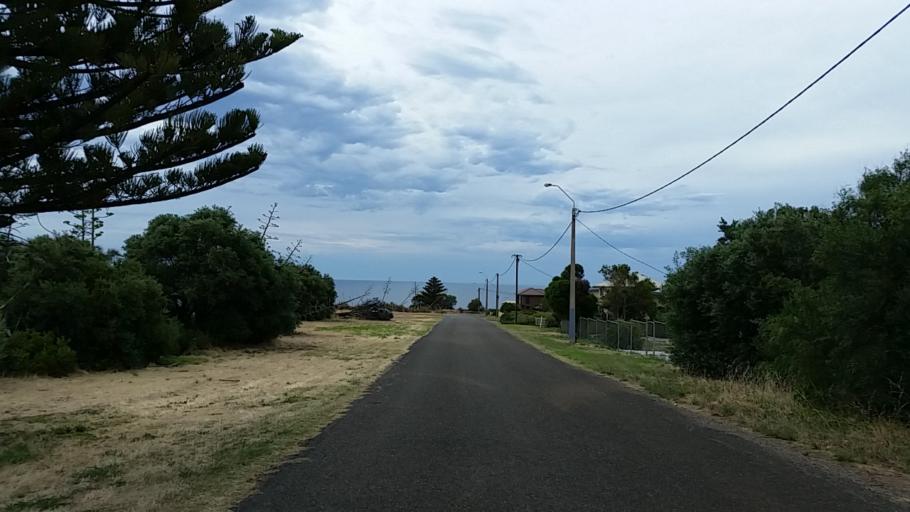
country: AU
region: South Australia
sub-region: Onkaparinga
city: Port Willunga
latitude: -35.3438
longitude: 138.4478
